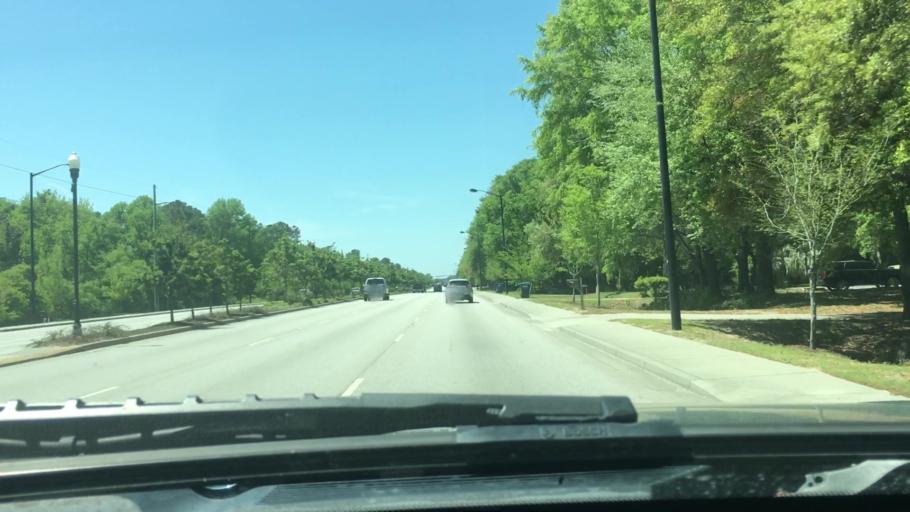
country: US
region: South Carolina
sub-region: Charleston County
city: Isle of Palms
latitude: 32.8681
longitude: -79.7822
